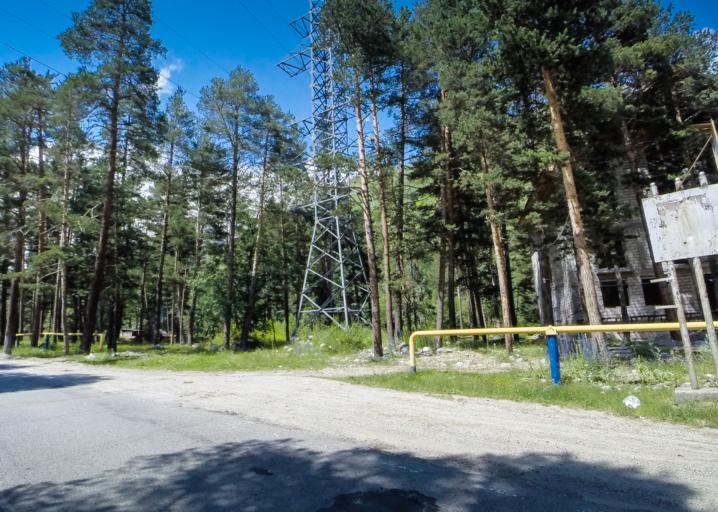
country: RU
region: Kabardino-Balkariya
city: Terskol
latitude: 43.2496
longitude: 42.5279
